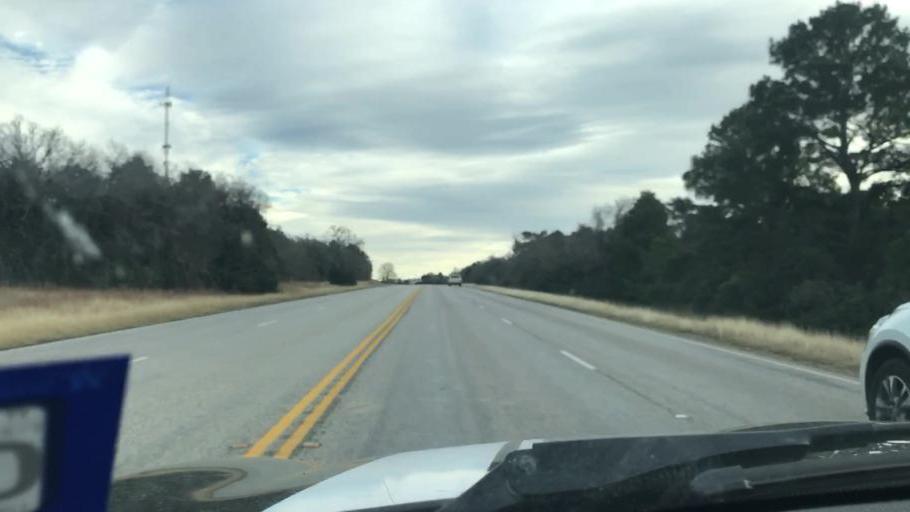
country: US
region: Texas
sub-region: Bastrop County
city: Camp Swift
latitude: 30.2525
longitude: -97.2254
